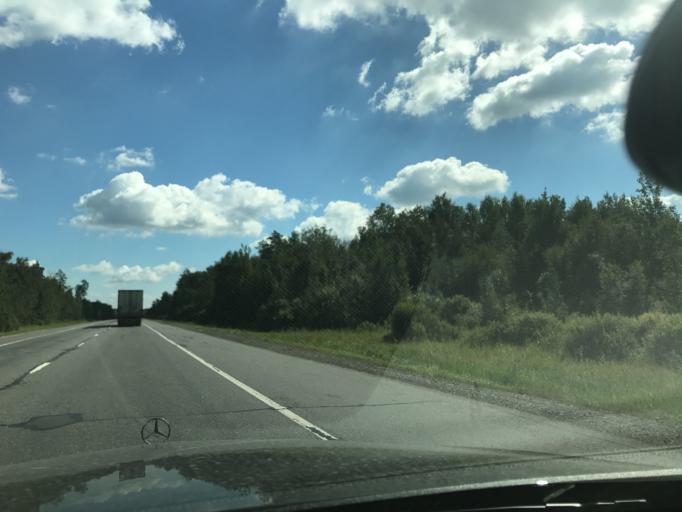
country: RU
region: Vladimir
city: Raduzhnyy
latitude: 56.0717
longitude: 40.2517
